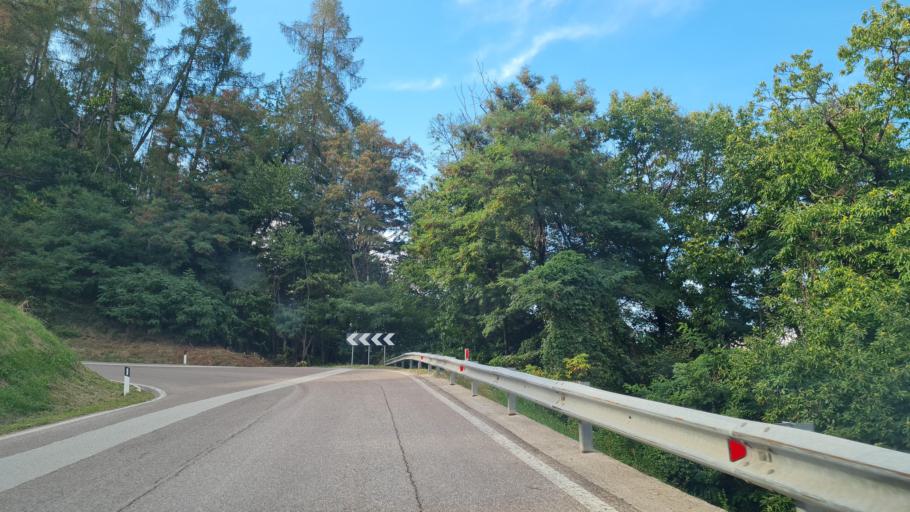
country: IT
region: Trentino-Alto Adige
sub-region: Provincia di Trento
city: Calceranica al Lago
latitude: 46.0083
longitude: 11.2347
